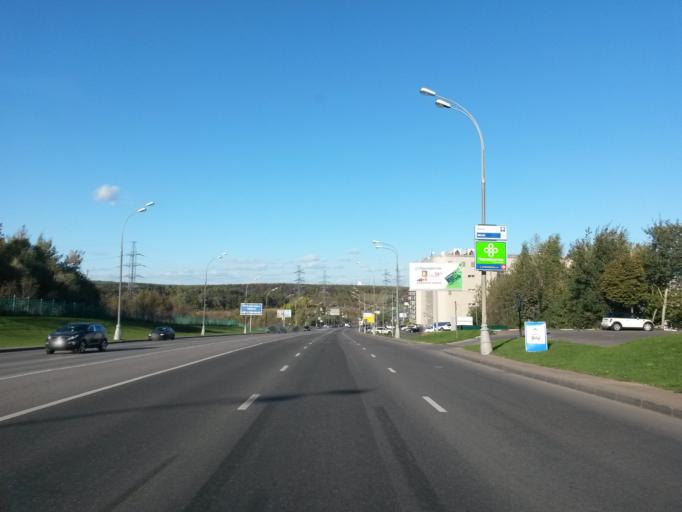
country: RU
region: Moscow
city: Chertanovo Yuzhnoye
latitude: 55.5727
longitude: 37.5634
